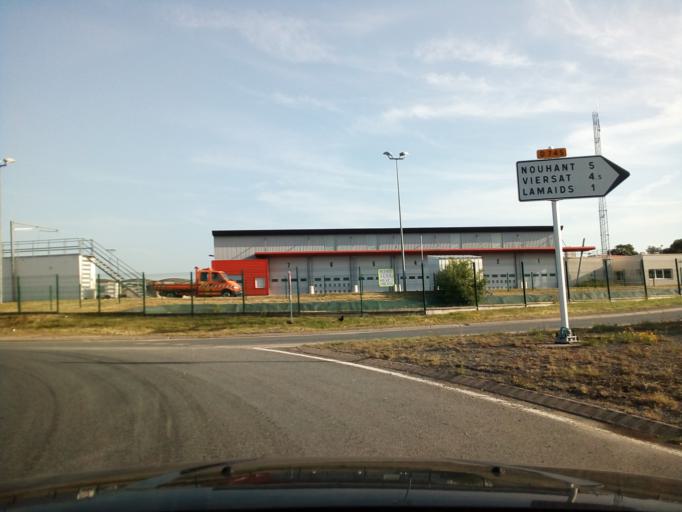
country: FR
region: Auvergne
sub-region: Departement de l'Allier
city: Huriel
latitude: 46.3076
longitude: 2.4458
